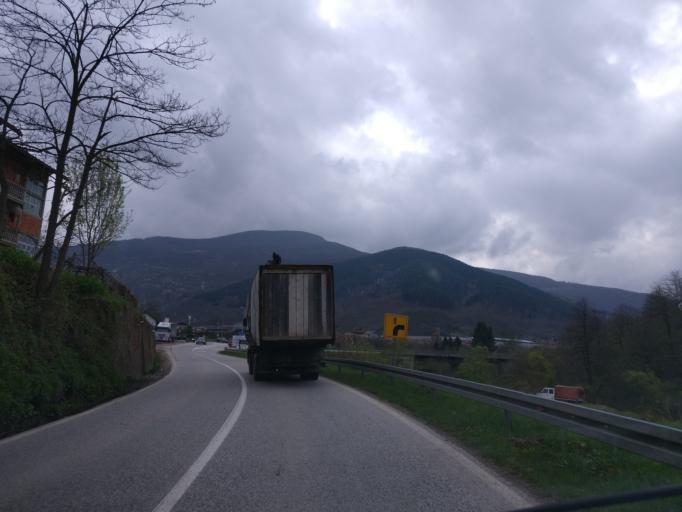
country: BA
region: Republika Srpska
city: Foca
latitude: 43.4925
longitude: 18.7412
